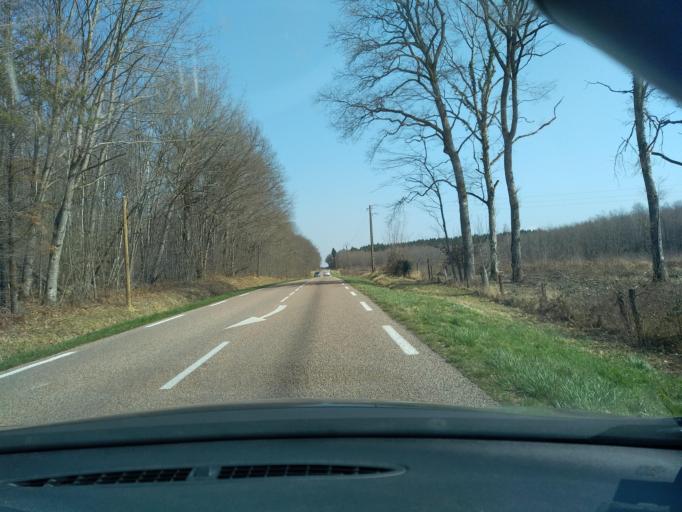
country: FR
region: Franche-Comte
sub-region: Departement du Jura
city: Mont-sous-Vaudrey
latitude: 46.9695
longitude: 5.5702
